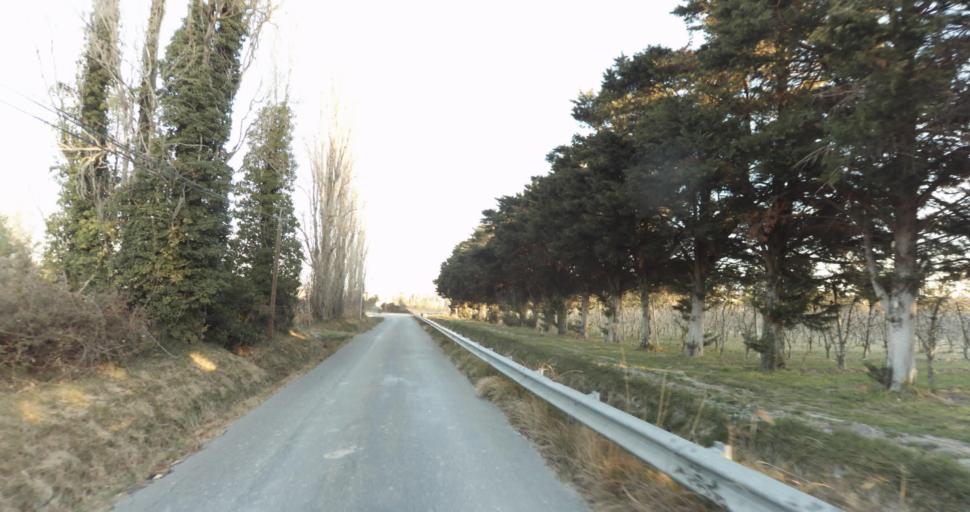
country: FR
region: Provence-Alpes-Cote d'Azur
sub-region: Departement des Bouches-du-Rhone
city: Barbentane
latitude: 43.8969
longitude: 4.7710
